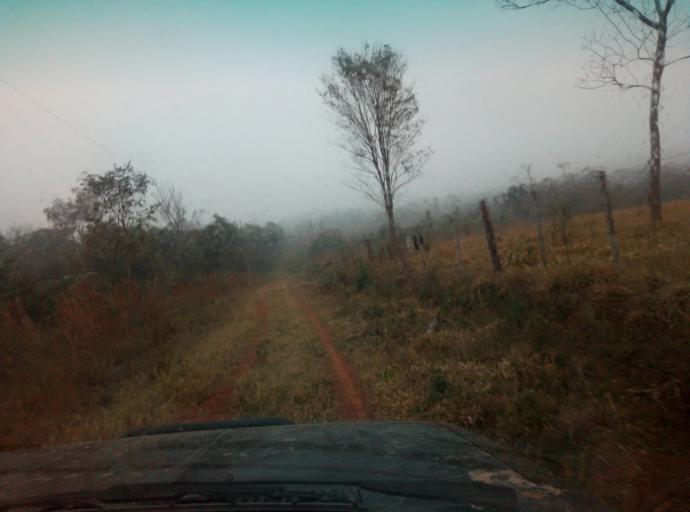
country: PY
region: Caaguazu
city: Doctor Cecilio Baez
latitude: -25.1513
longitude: -56.2607
